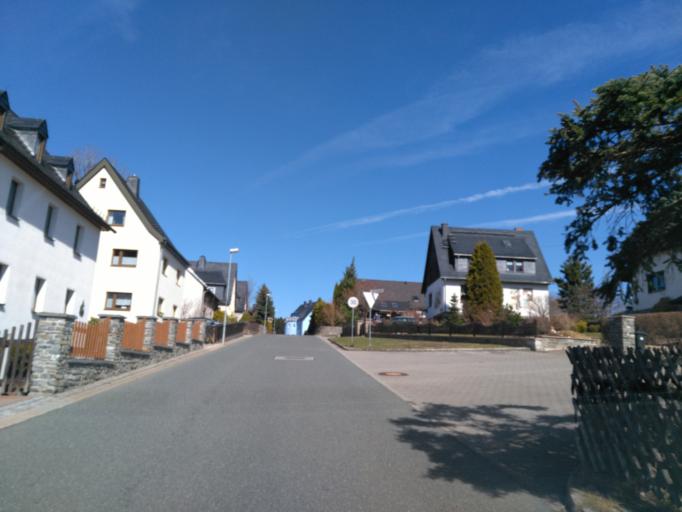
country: DE
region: Saxony
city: Breitenbrunn
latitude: 50.4777
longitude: 12.7642
